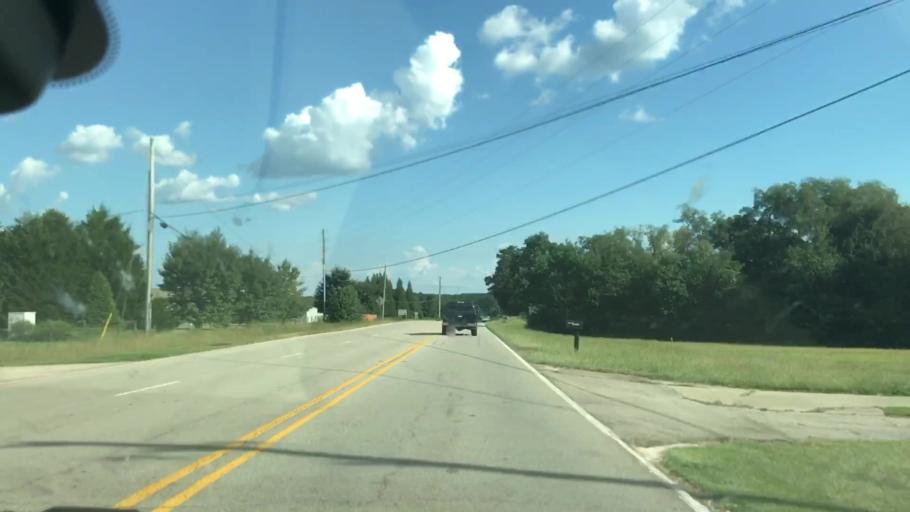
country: US
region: Georgia
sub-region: Troup County
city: La Grange
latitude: 32.9760
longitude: -84.9896
